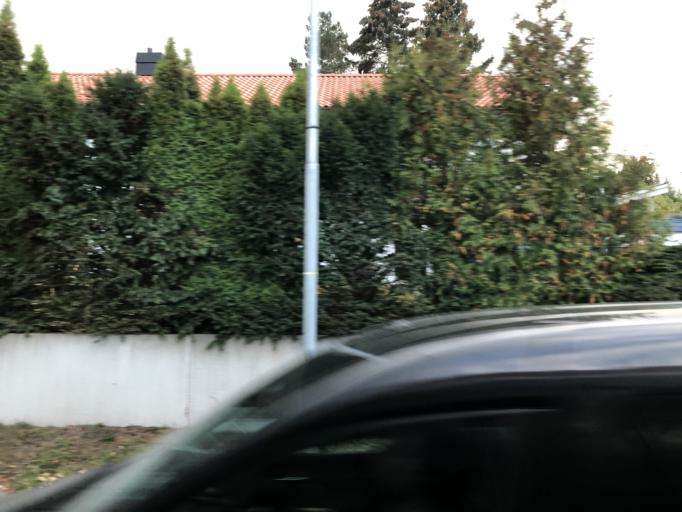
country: SE
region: Stockholm
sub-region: Jarfalla Kommun
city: Jakobsberg
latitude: 59.4297
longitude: 17.8172
